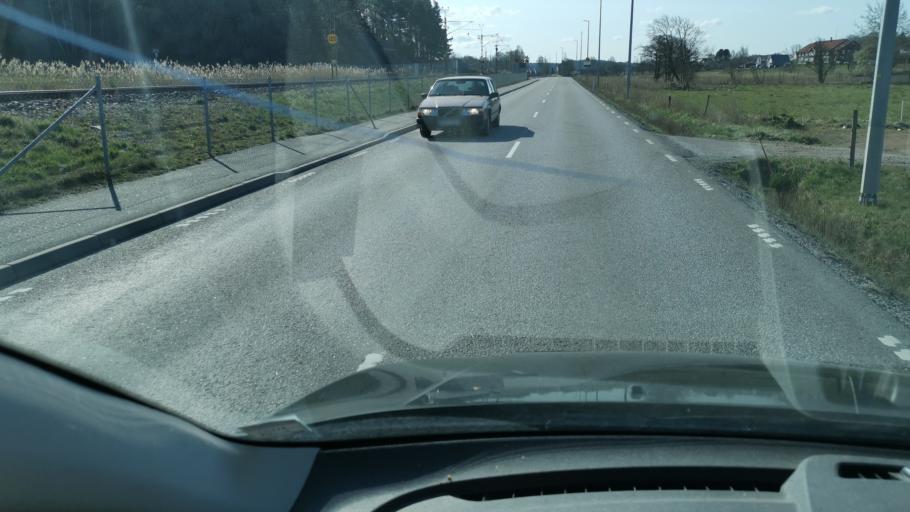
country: SE
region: Vaestra Goetaland
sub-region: Kungalvs Kommun
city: Kungalv
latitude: 57.8087
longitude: 11.9086
